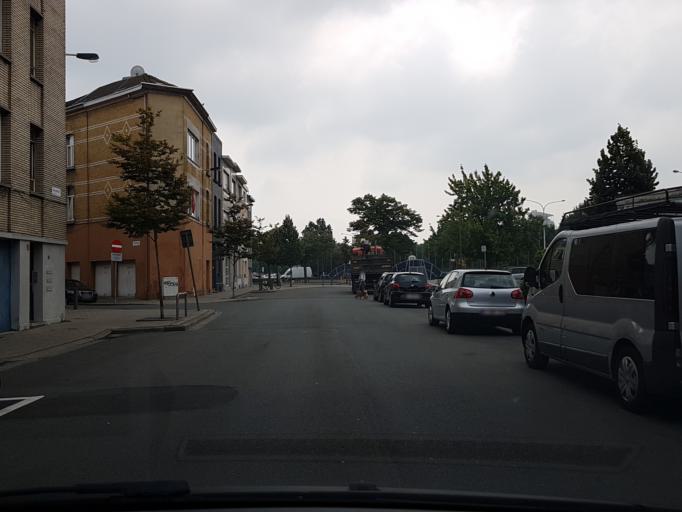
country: BE
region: Flanders
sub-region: Provincie Antwerpen
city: Antwerpen
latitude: 51.1983
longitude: 4.3923
